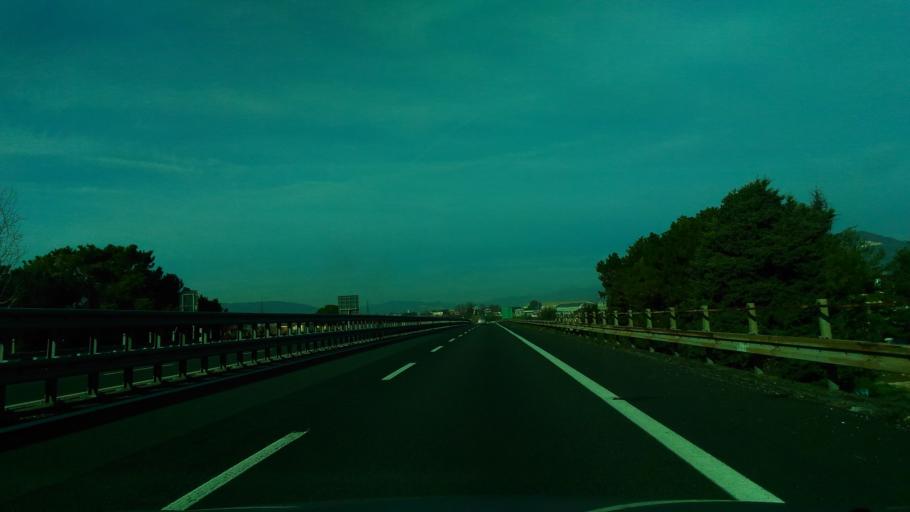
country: IT
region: Tuscany
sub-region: Provincia di Massa-Carrara
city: Massa
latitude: 44.0284
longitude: 10.0917
